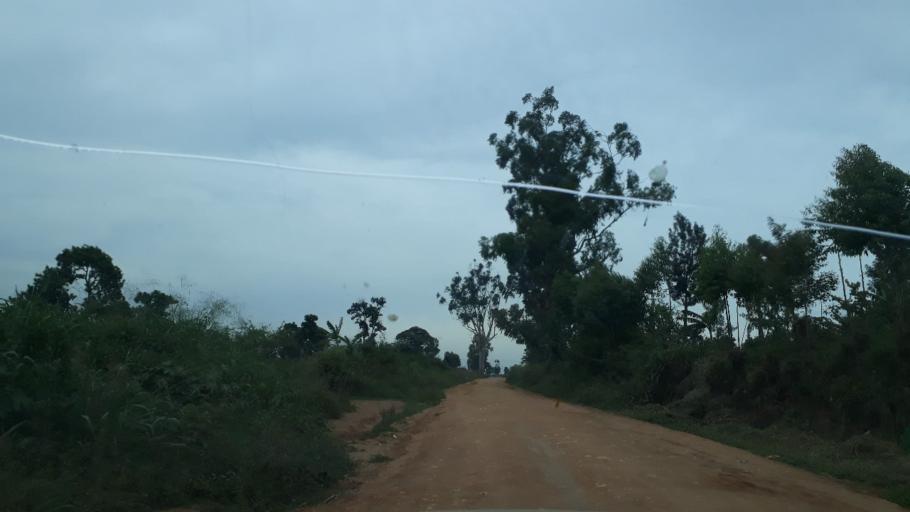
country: UG
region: Northern Region
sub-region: Zombo District
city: Paidha
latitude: 2.0567
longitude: 30.6316
